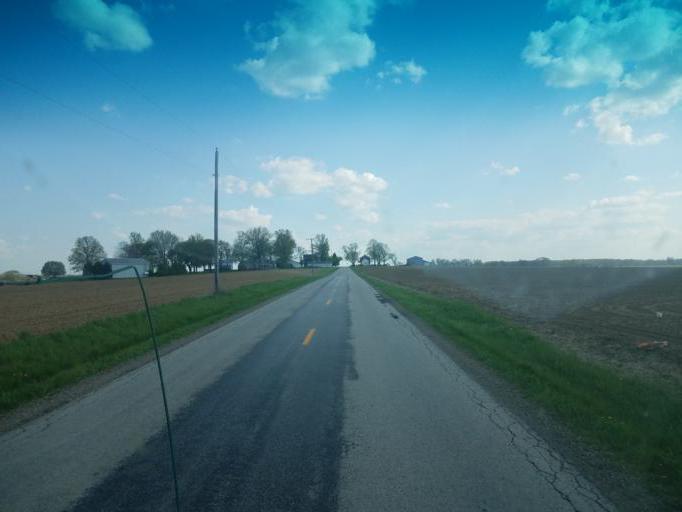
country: US
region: Ohio
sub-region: Wayne County
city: Smithville
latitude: 40.8533
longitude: -81.8780
